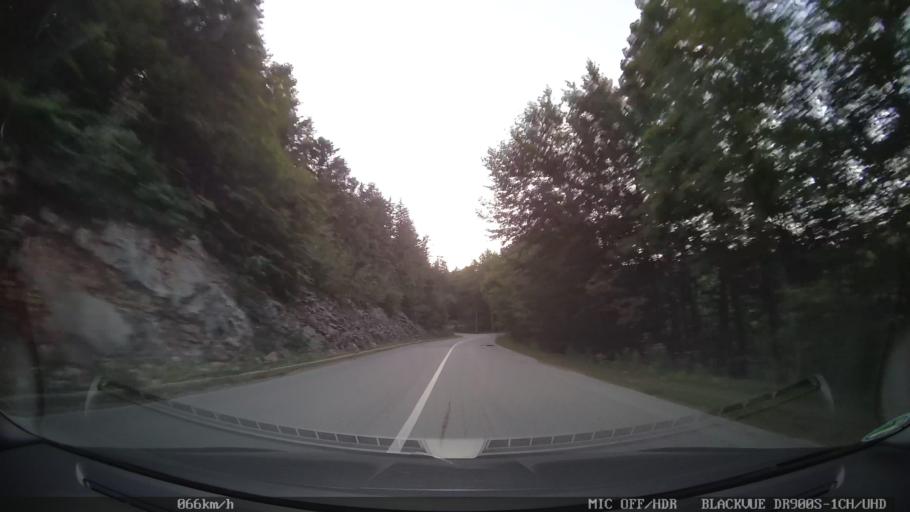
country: HR
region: Primorsko-Goranska
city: Novi Vinodolski
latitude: 45.1904
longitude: 14.9095
